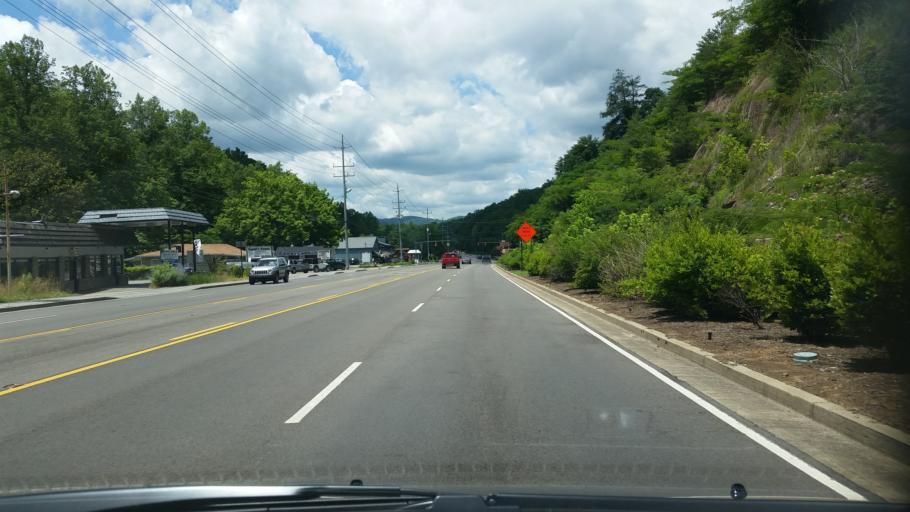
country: US
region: Tennessee
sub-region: Sevier County
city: Gatlinburg
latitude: 35.7261
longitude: -83.4679
